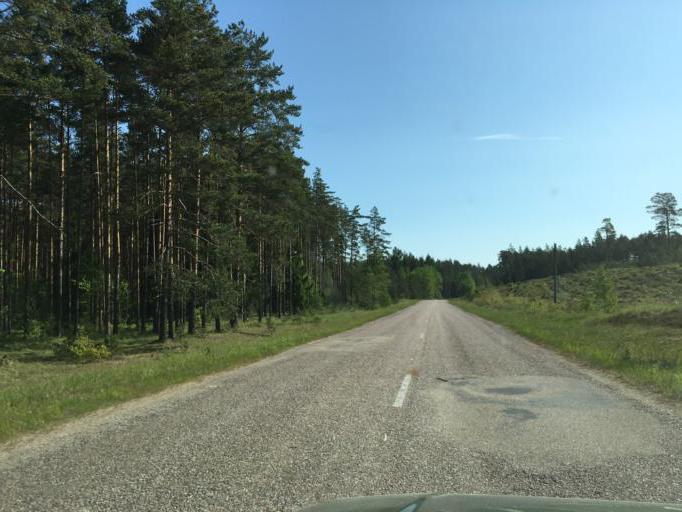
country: LV
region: Ventspils
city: Ventspils
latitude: 57.5129
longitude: 21.8664
